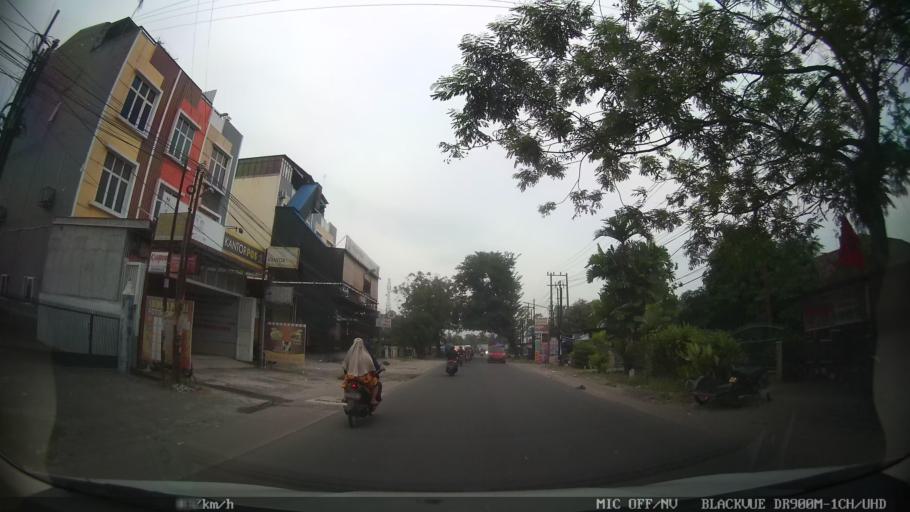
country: ID
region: North Sumatra
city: Medan
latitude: 3.5527
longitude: 98.7044
